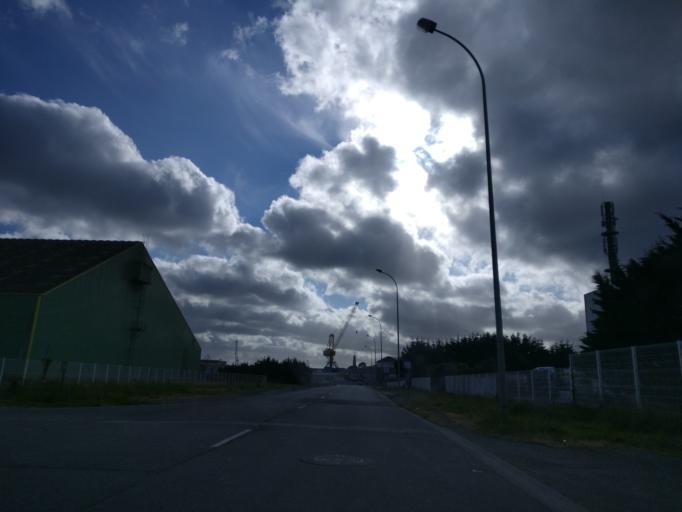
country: FR
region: Brittany
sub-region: Departement du Finistere
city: Brest
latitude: 48.3856
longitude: -4.4705
